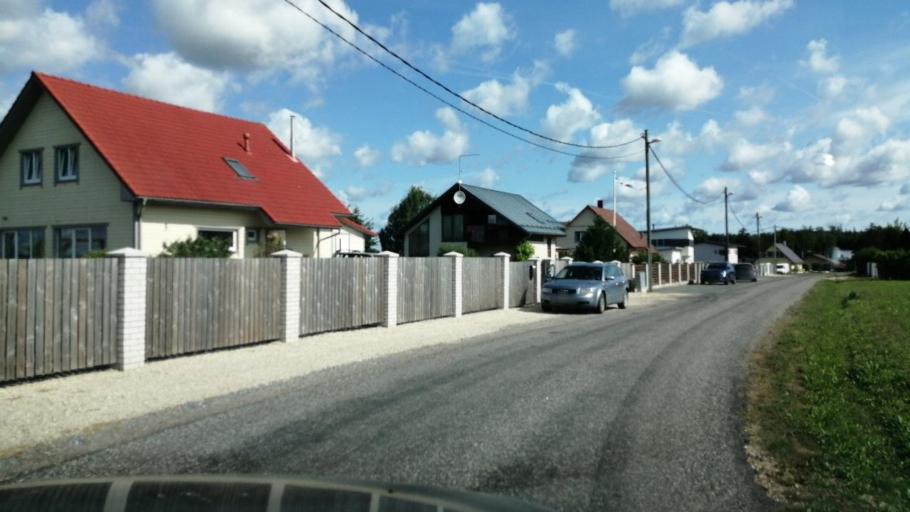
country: EE
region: Viljandimaa
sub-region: Viiratsi vald
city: Viiratsi
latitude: 58.3644
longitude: 25.6443
